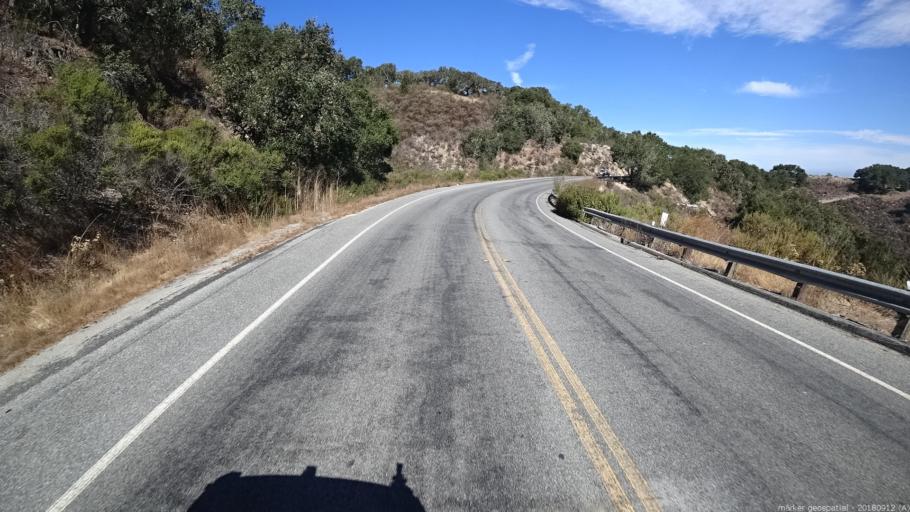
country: US
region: California
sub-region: Monterey County
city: Carmel Valley Village
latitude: 36.5322
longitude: -121.7496
